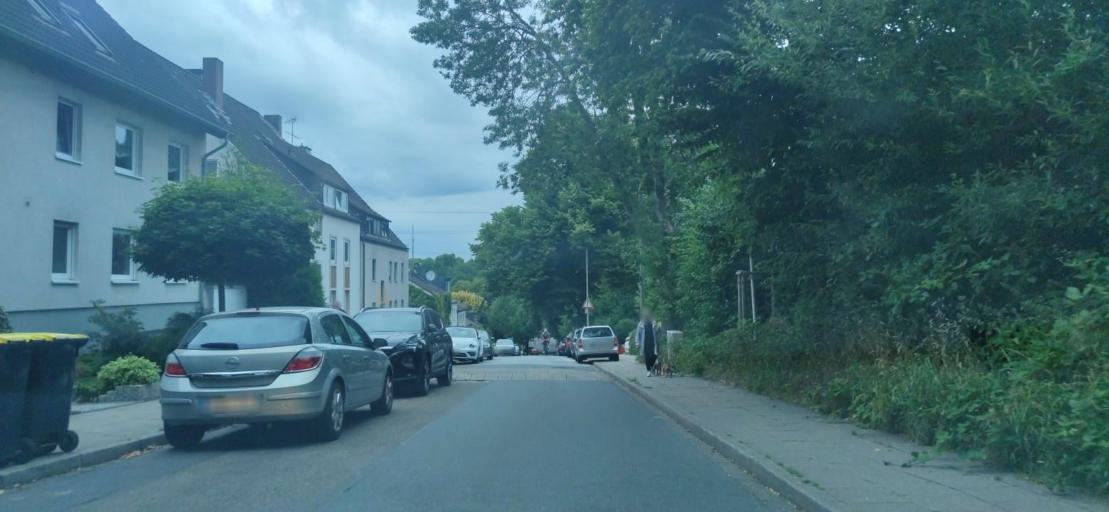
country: DE
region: North Rhine-Westphalia
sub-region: Regierungsbezirk Dusseldorf
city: Essen
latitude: 51.4227
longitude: 7.0794
